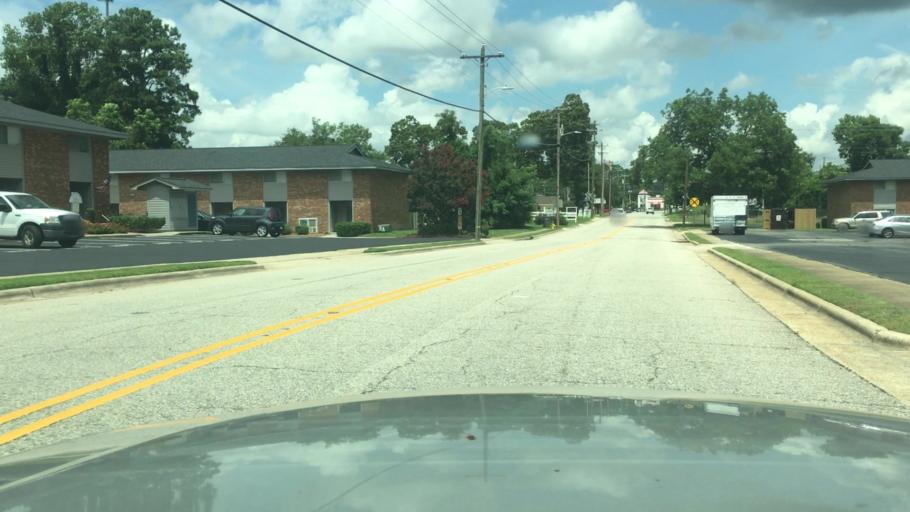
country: US
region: North Carolina
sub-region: Cumberland County
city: Fayetteville
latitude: 35.0423
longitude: -78.9286
